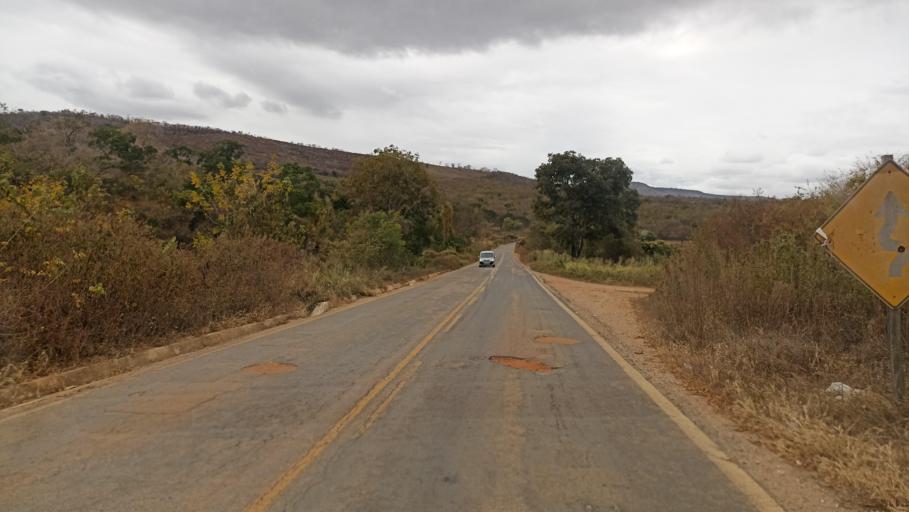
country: BR
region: Minas Gerais
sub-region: Itinga
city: Itinga
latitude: -16.6482
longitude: -41.8294
